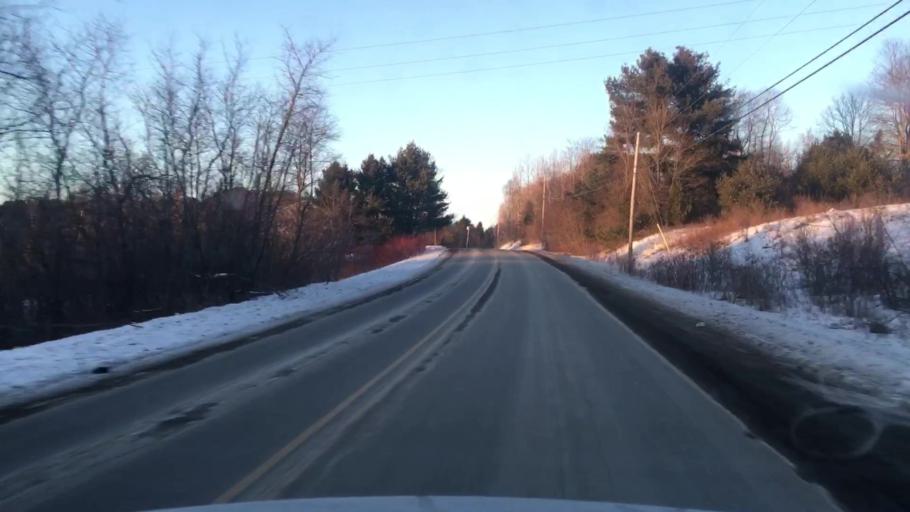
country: US
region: Maine
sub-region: Penobscot County
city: Brewer
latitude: 44.7396
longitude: -68.7651
